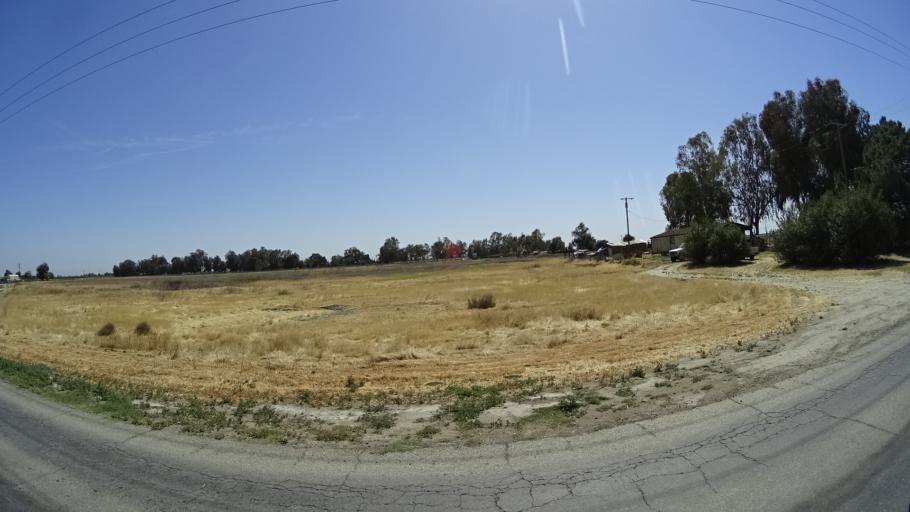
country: US
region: California
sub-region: Kings County
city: Stratford
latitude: 36.1981
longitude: -119.7983
